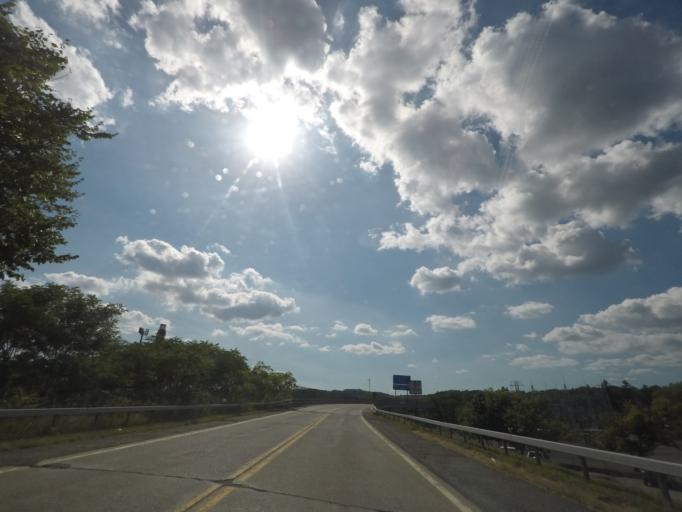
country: US
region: New York
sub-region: Albany County
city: Watervliet
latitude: 42.7205
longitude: -73.7127
